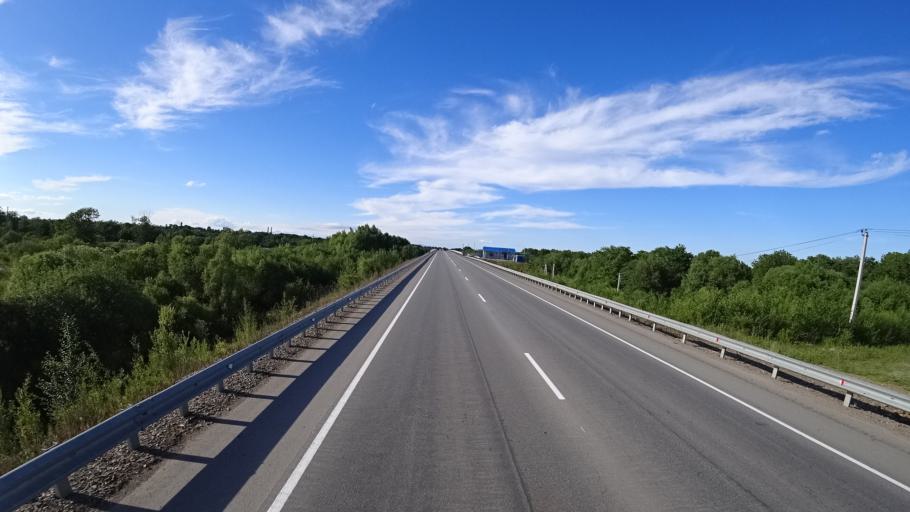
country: RU
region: Khabarovsk Krai
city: Khor
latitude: 47.8615
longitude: 134.9631
